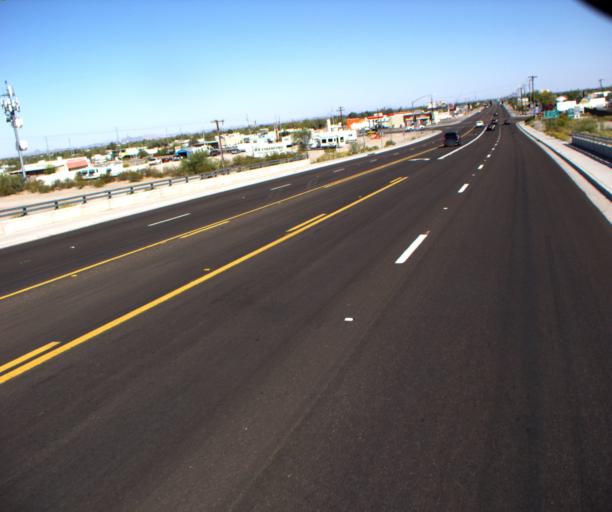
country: US
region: Arizona
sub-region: La Paz County
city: Quartzsite
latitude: 33.6647
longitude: -114.2170
